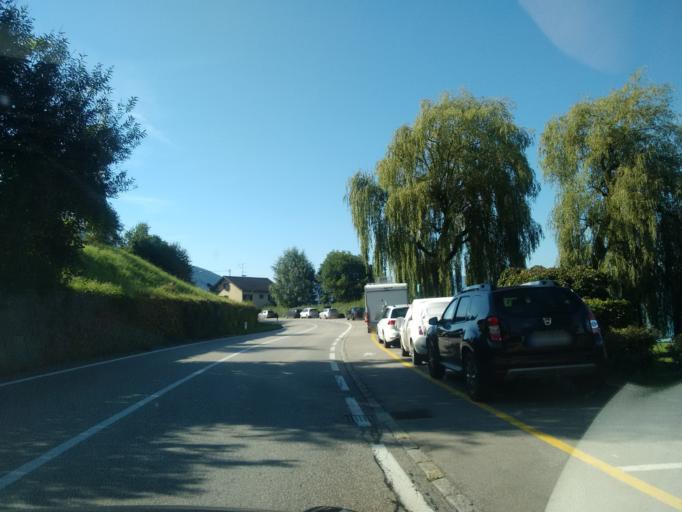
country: AT
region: Upper Austria
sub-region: Politischer Bezirk Vocklabruck
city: Attersee
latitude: 47.8863
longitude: 13.5690
